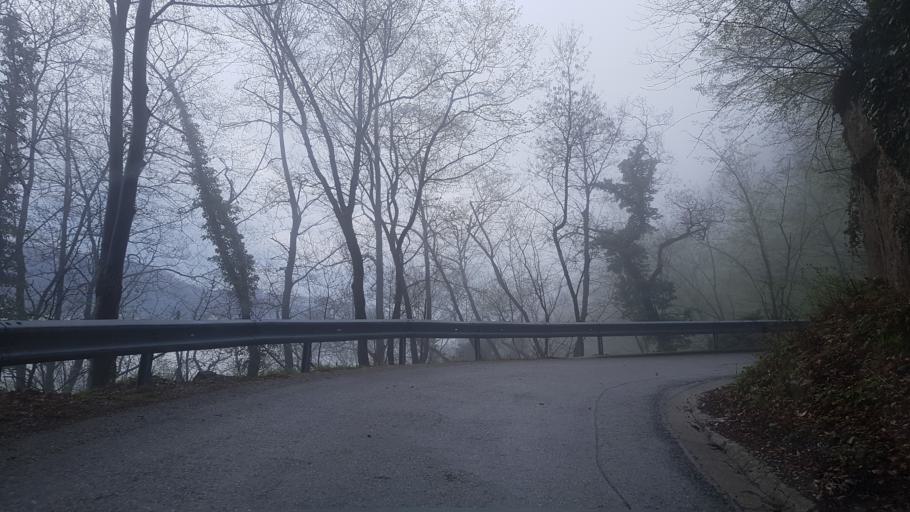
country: SI
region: Tolmin
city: Tolmin
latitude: 46.1183
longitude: 13.7956
